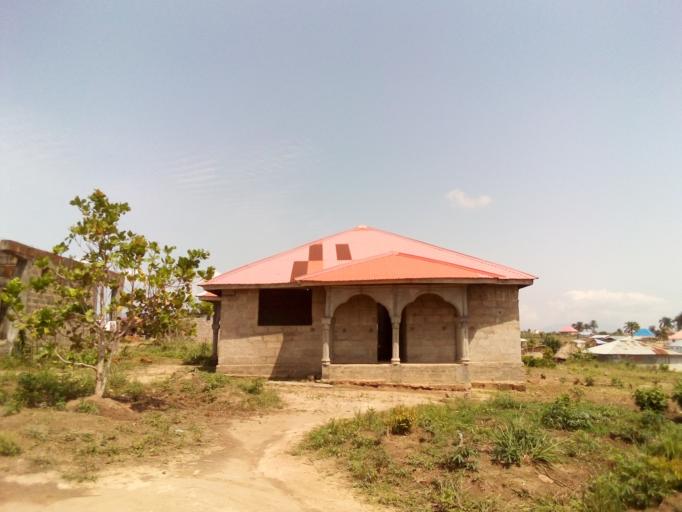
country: SL
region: Western Area
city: Waterloo
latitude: 8.3457
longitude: -13.0188
